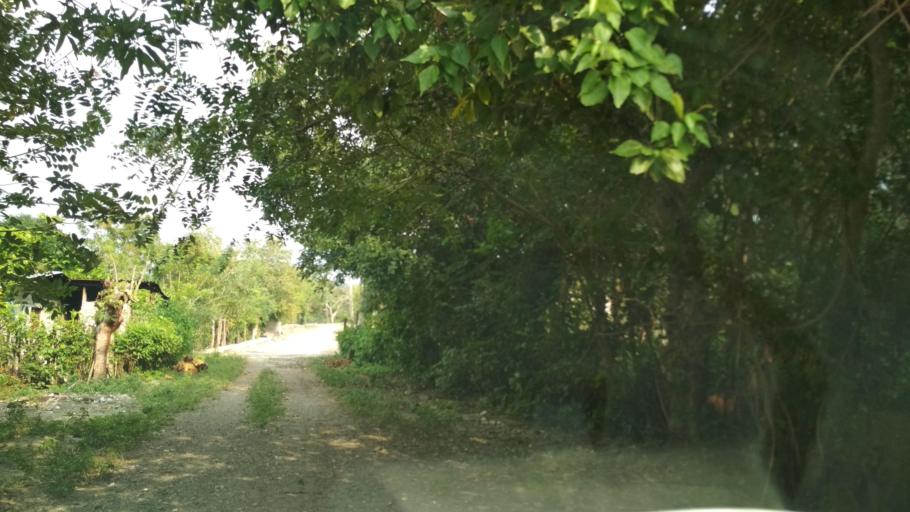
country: MM
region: Kayah
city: Loikaw
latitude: 20.2352
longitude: 97.2773
